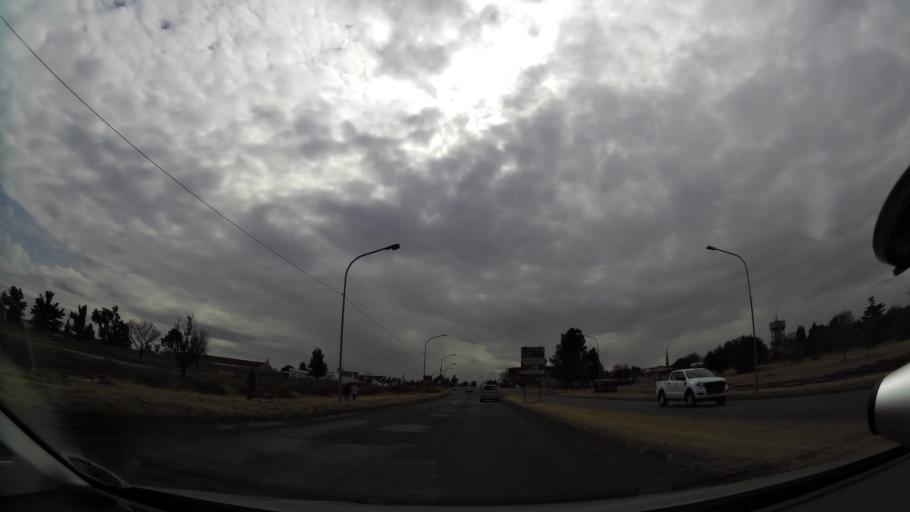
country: ZA
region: Orange Free State
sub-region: Fezile Dabi District Municipality
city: Kroonstad
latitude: -27.6517
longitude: 27.2314
